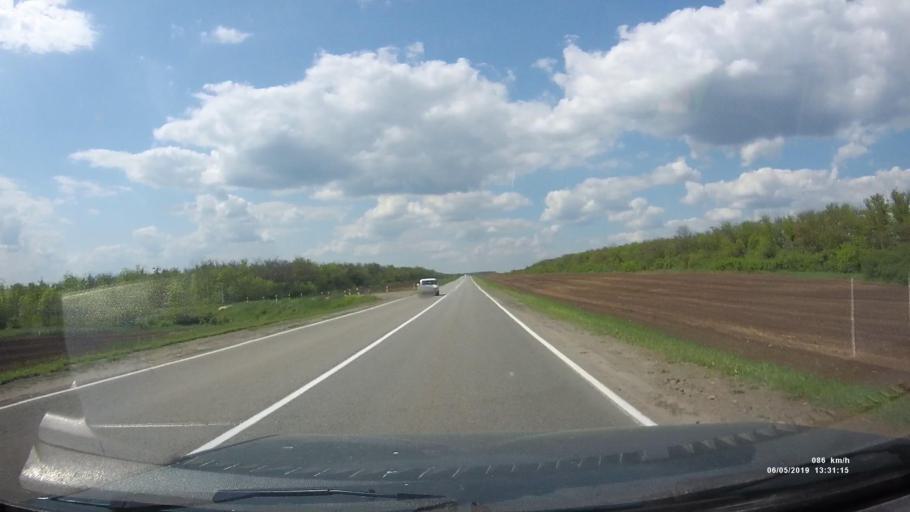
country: RU
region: Rostov
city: Ust'-Donetskiy
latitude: 47.6754
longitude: 40.8133
